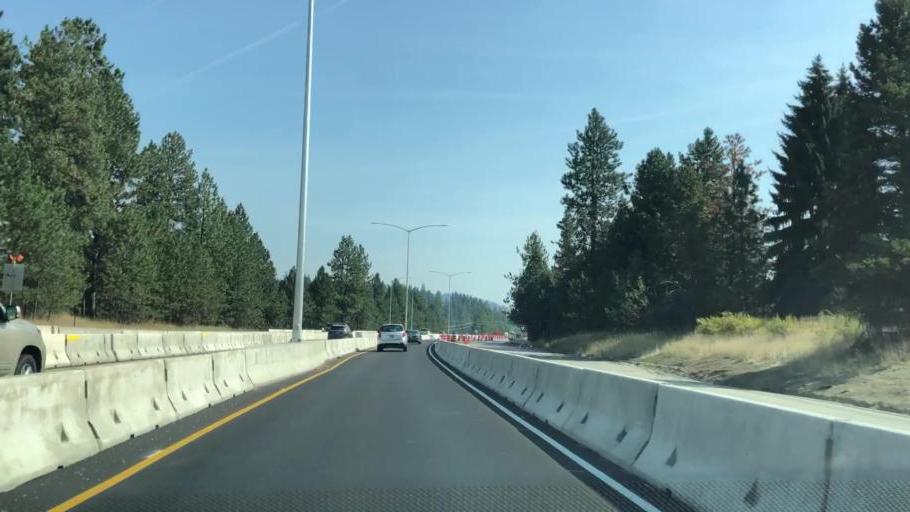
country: US
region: Idaho
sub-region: Kootenai County
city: Coeur d'Alene
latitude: 47.6942
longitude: -116.7706
